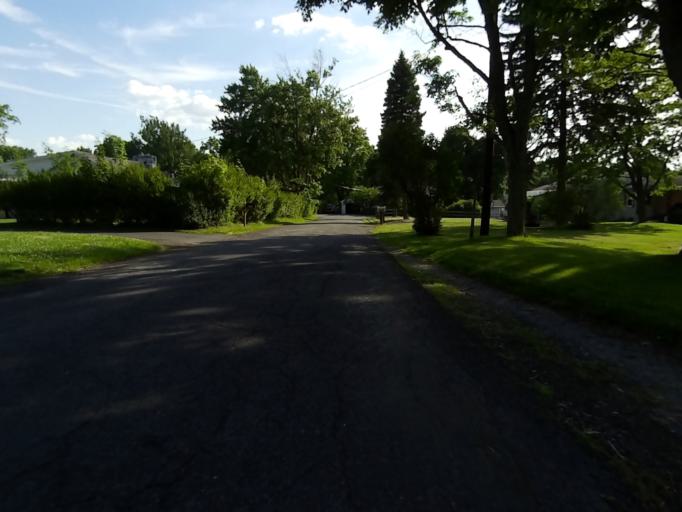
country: US
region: Pennsylvania
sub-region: Centre County
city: Park Forest Village
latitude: 40.7997
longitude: -77.9542
